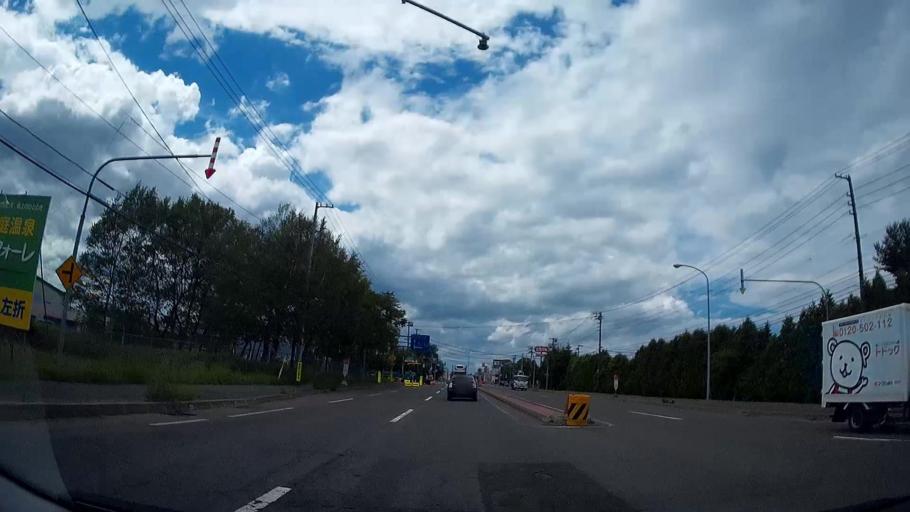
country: JP
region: Hokkaido
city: Chitose
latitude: 42.8684
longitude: 141.5908
